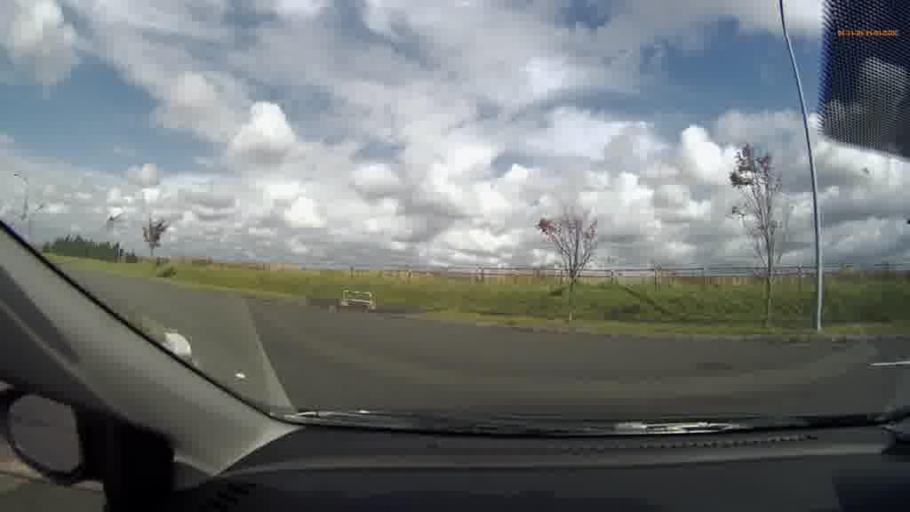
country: JP
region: Hokkaido
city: Kushiro
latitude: 43.0293
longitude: 144.4088
